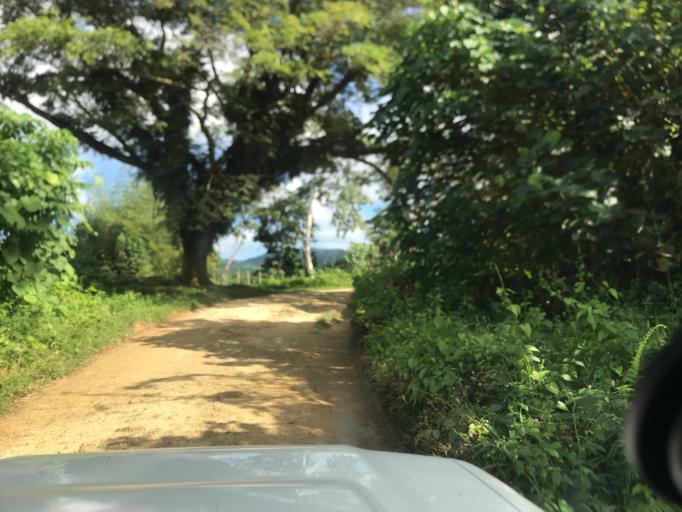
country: VU
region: Sanma
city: Luganville
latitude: -15.4674
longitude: 167.0723
